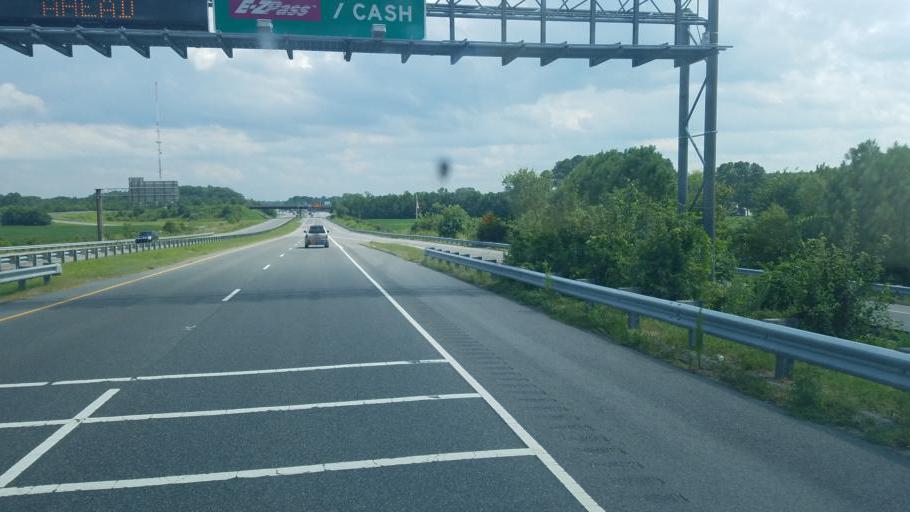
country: US
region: North Carolina
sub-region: Currituck County
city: Moyock
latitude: 36.6154
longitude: -76.2103
